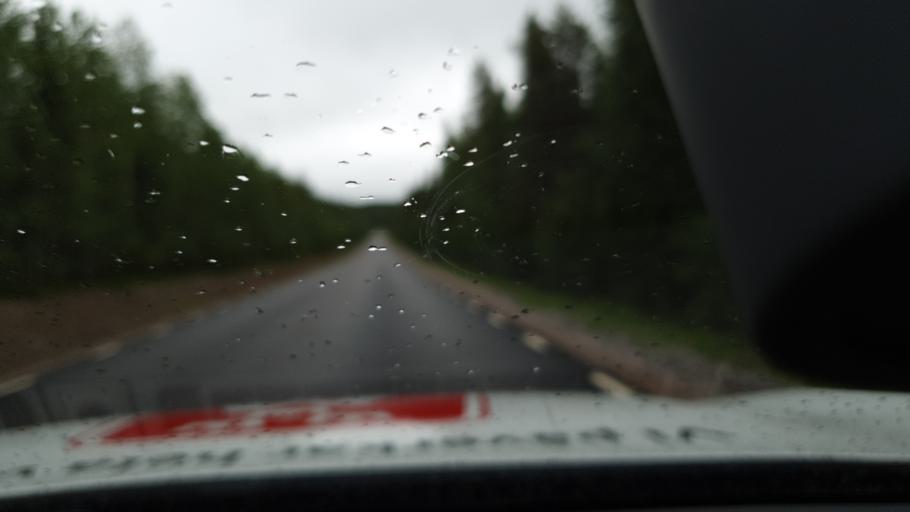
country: SE
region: Norrbotten
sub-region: Overtornea Kommun
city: OEvertornea
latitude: 66.4718
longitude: 23.4688
